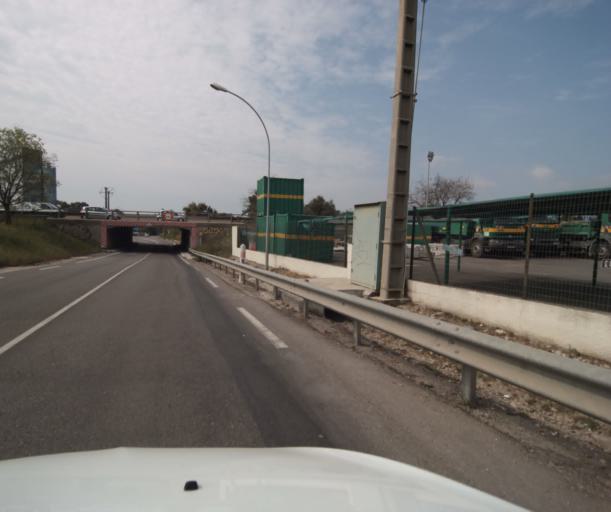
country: FR
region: Provence-Alpes-Cote d'Azur
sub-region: Departement du Var
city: La Farlede
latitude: 43.1444
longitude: 6.0327
